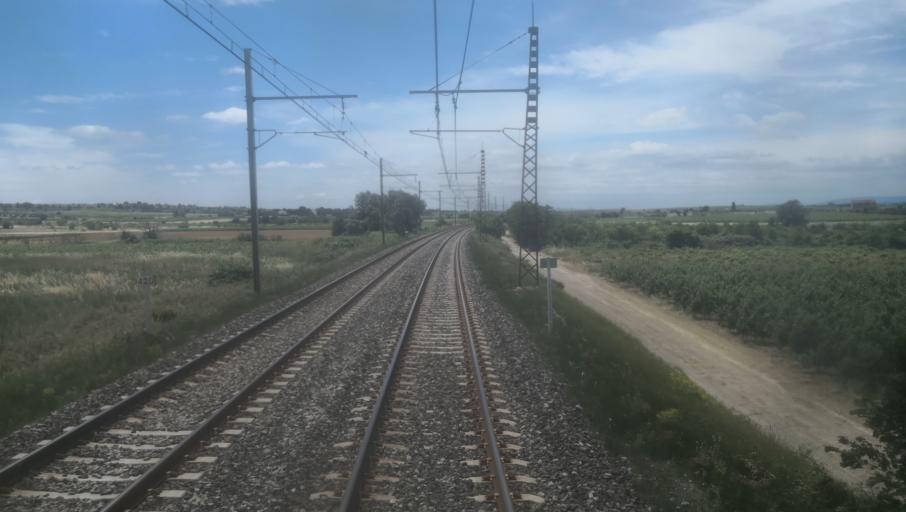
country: FR
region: Languedoc-Roussillon
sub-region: Departement de l'Herault
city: Nissan-lez-Enserune
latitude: 43.2864
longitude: 3.1050
